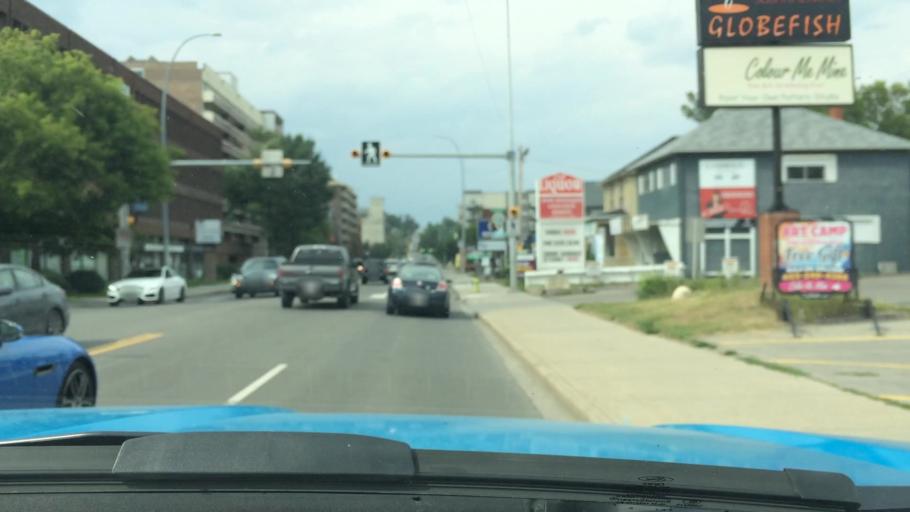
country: CA
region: Alberta
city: Calgary
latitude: 51.0544
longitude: -114.0946
